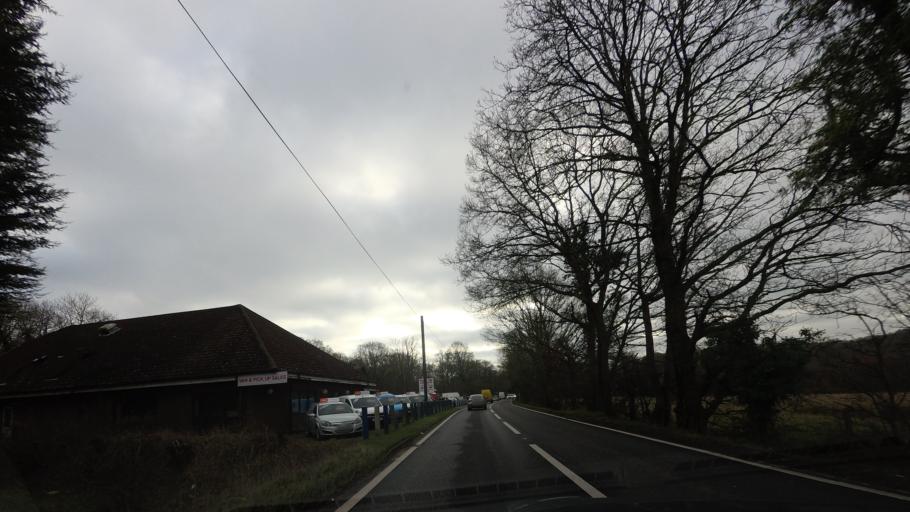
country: GB
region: England
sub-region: East Sussex
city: Wadhurst
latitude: 51.0791
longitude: 0.4186
